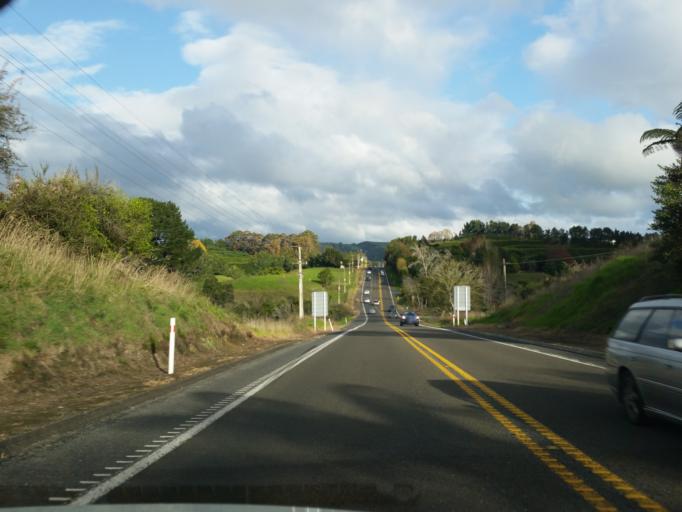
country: NZ
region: Bay of Plenty
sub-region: Tauranga City
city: Tauranga
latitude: -37.6706
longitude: 176.0216
